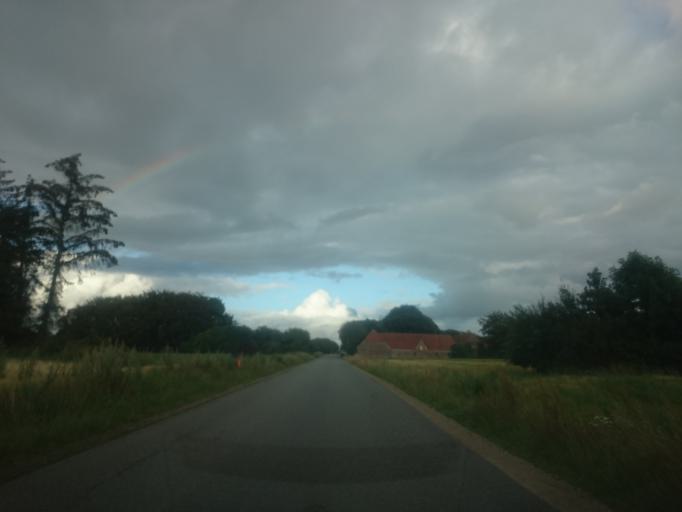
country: DK
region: South Denmark
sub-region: Billund Kommune
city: Grindsted
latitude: 55.6484
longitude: 8.8304
